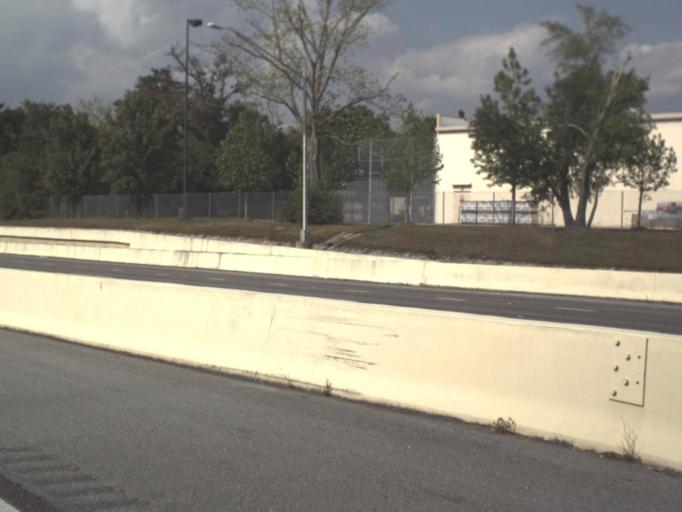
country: US
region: Florida
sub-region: Escambia County
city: Brent
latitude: 30.4753
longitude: -87.2290
